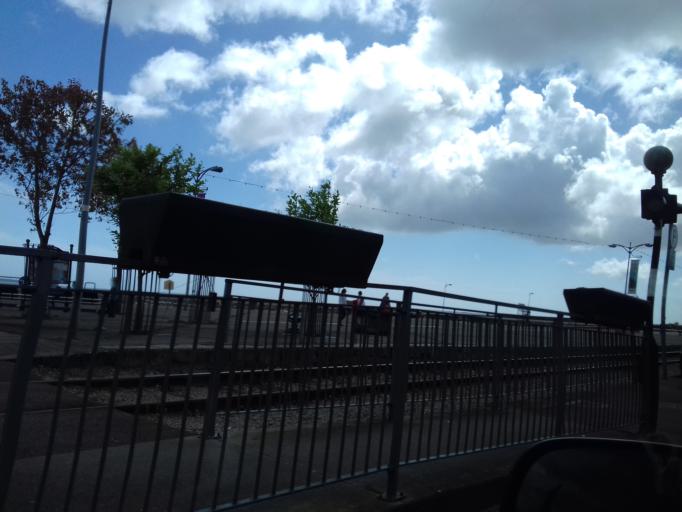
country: IE
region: Leinster
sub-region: Loch Garman
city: Loch Garman
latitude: 52.3388
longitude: -6.4596
